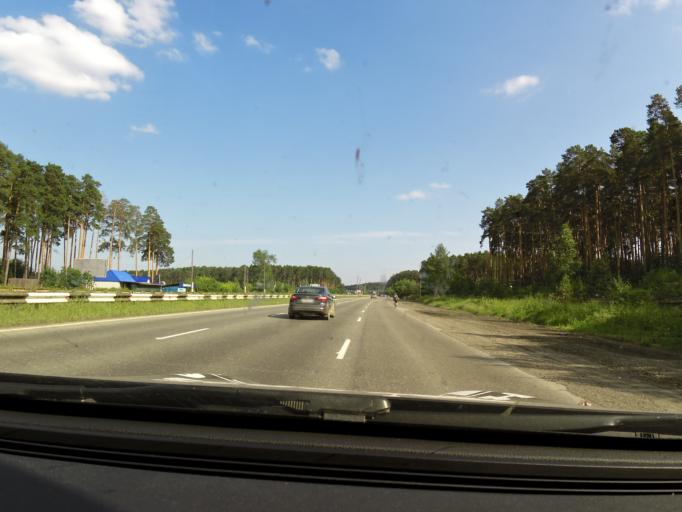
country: RU
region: Sverdlovsk
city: Shirokaya Rechka
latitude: 56.8178
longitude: 60.5086
